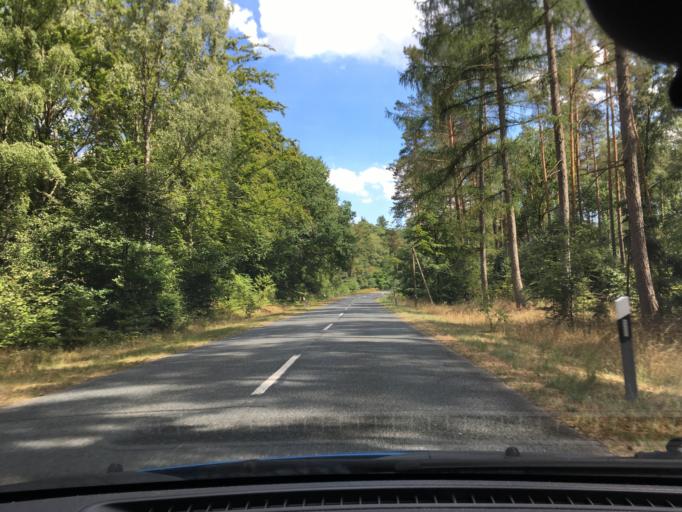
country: DE
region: Lower Saxony
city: Rehlingen
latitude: 53.0805
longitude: 10.2242
